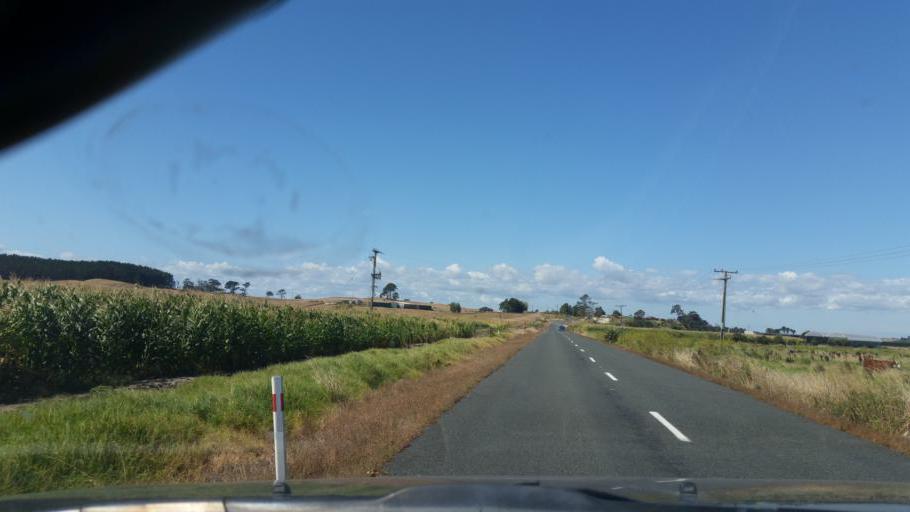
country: NZ
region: Northland
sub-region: Kaipara District
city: Dargaville
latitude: -35.9484
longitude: 173.8057
